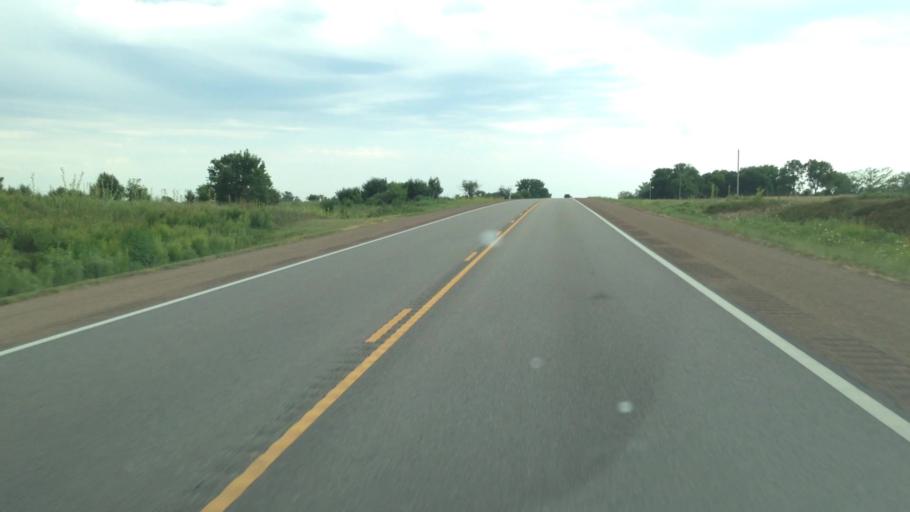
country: US
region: Kansas
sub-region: Woodson County
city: Yates Center
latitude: 38.0083
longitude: -95.7390
